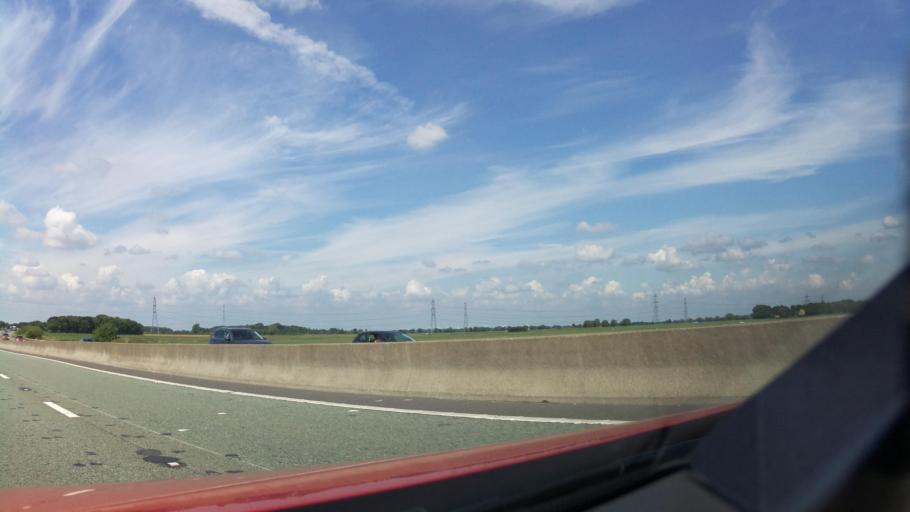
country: GB
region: England
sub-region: North Lincolnshire
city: Gunness
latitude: 53.5550
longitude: -0.7557
